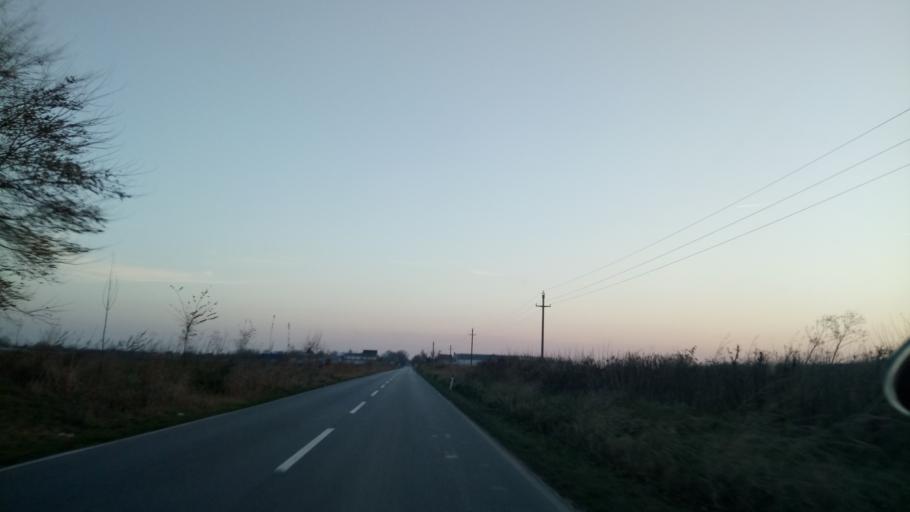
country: RS
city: Belegis
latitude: 45.0328
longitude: 20.3343
